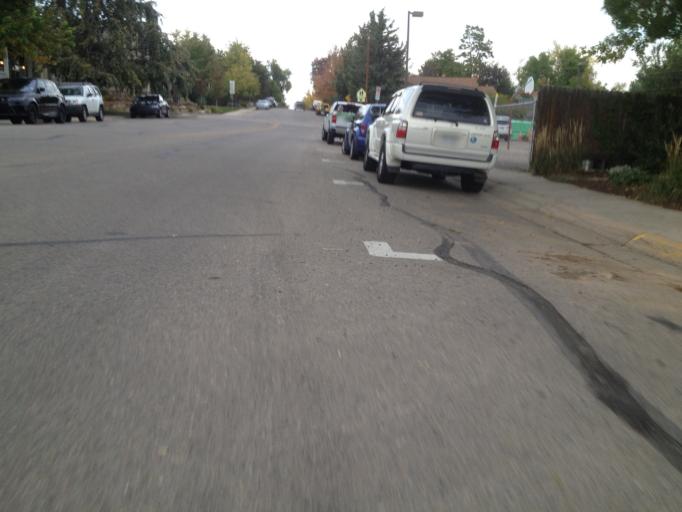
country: US
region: Colorado
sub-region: Boulder County
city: Louisville
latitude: 39.9791
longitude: -105.1369
